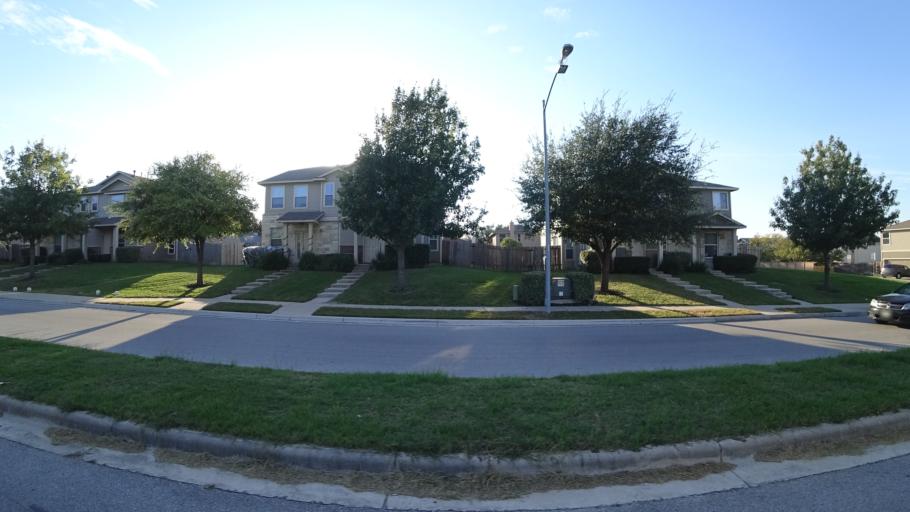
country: US
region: Texas
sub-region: Travis County
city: Pflugerville
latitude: 30.4151
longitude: -97.6462
